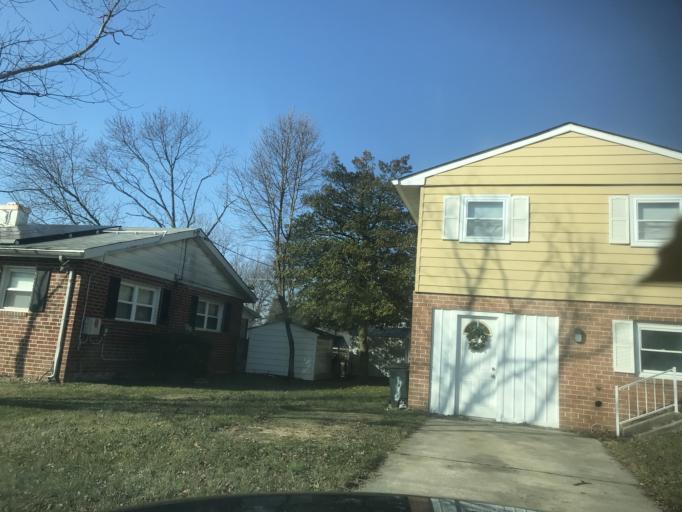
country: US
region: Maryland
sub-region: Baltimore County
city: Woodlawn
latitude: 39.2988
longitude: -76.7400
